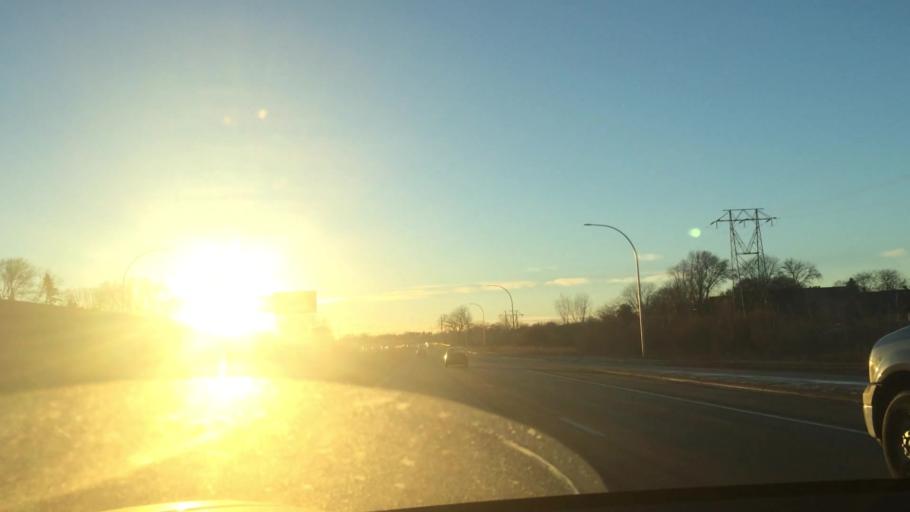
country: US
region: Minnesota
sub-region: Hennepin County
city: Robbinsdale
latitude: 45.0408
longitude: -93.3337
